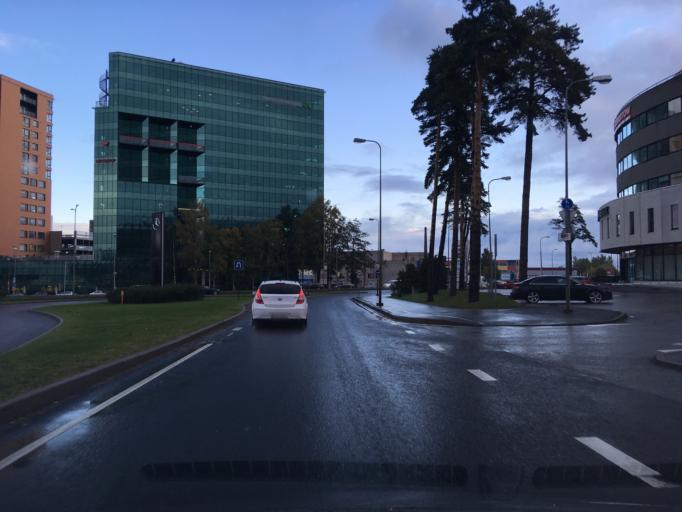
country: EE
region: Harju
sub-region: Tallinna linn
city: Tallinn
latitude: 59.4027
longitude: 24.7334
